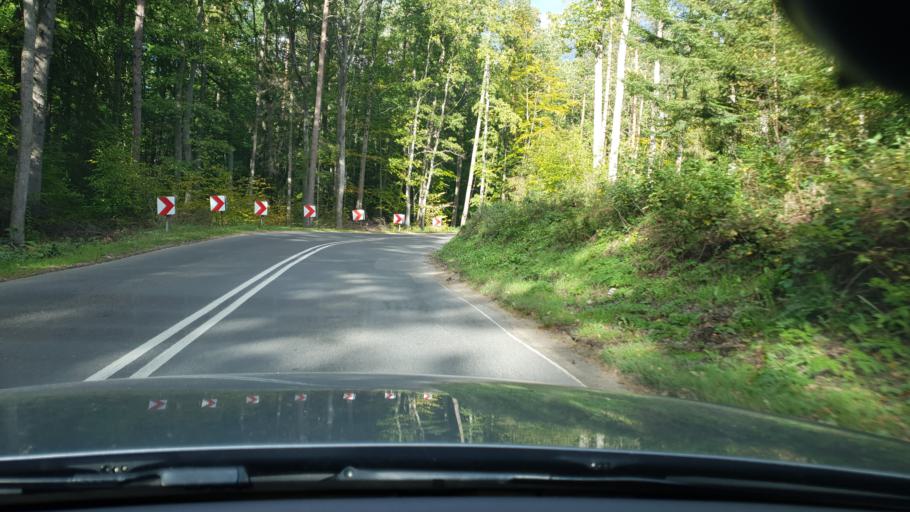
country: PL
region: Pomeranian Voivodeship
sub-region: Powiat wejherowski
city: Koleczkowo
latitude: 54.4982
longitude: 18.3613
